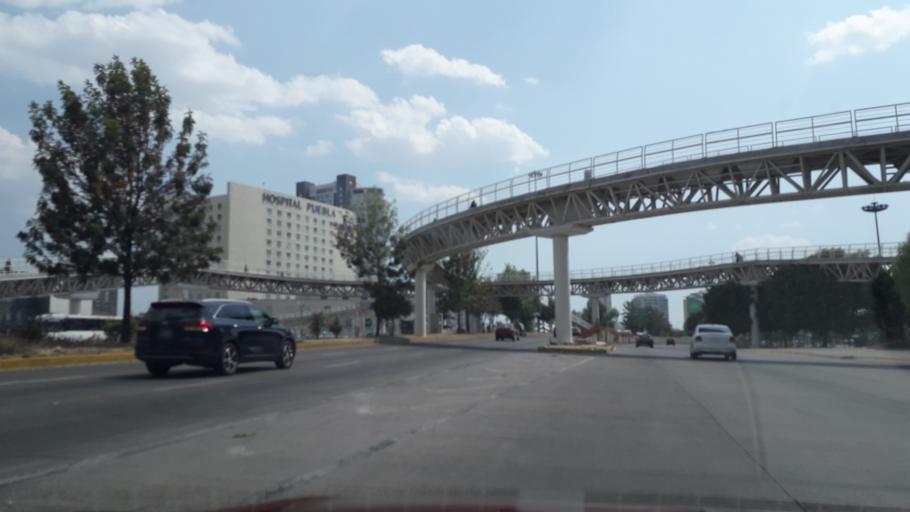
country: MX
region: Puebla
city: Puebla
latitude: 19.0328
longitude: -98.2285
